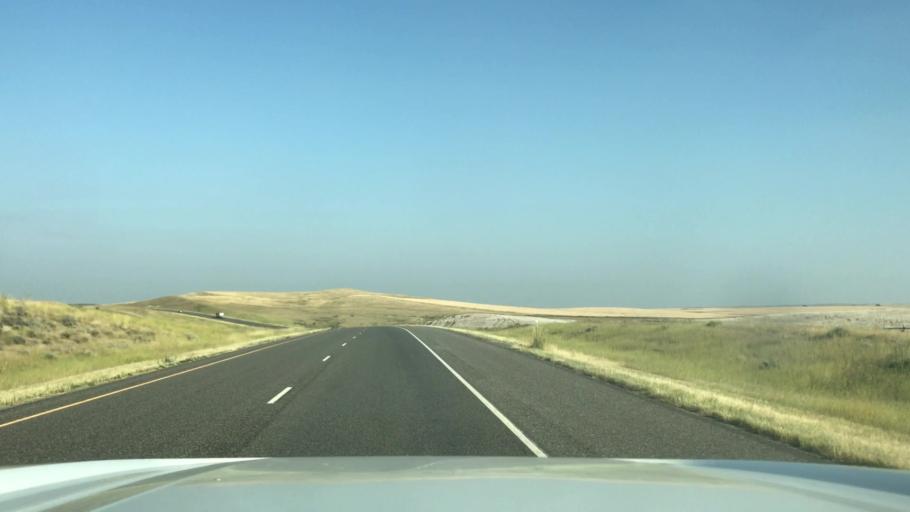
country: US
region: Montana
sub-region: Big Horn County
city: Hardin
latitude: 45.7696
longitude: -107.9323
